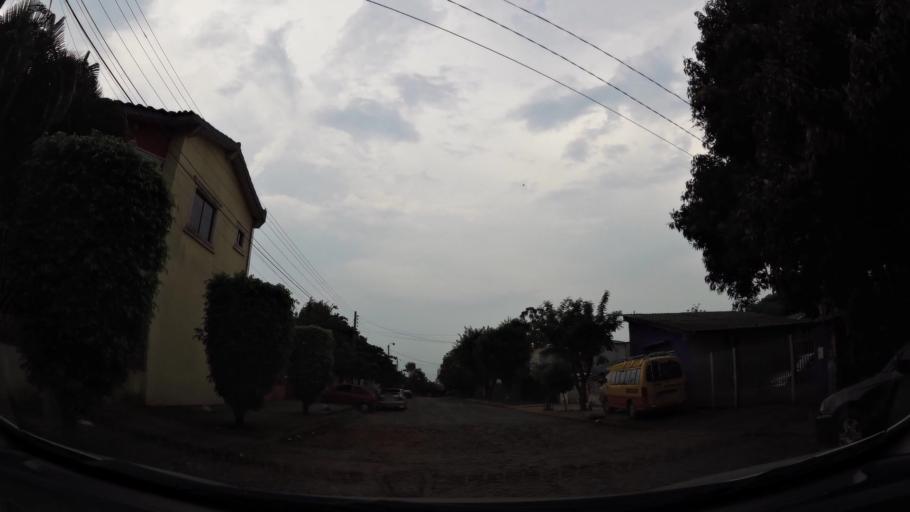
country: PY
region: Alto Parana
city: Presidente Franco
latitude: -25.5389
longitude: -54.6032
